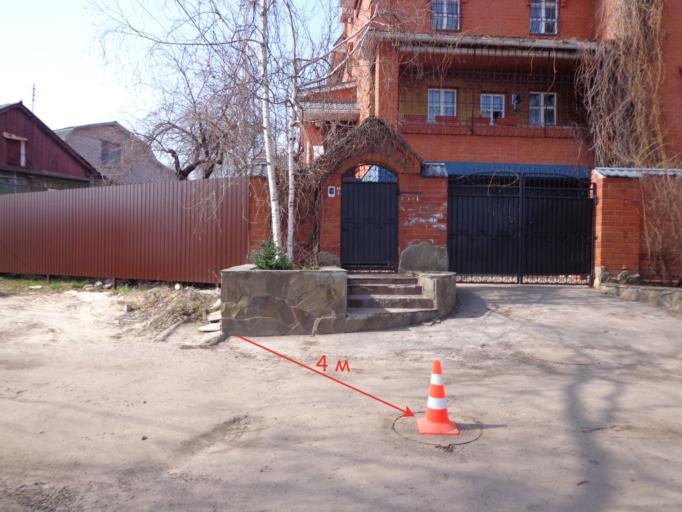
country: RU
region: Voronezj
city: Voronezh
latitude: 51.7054
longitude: 39.2351
